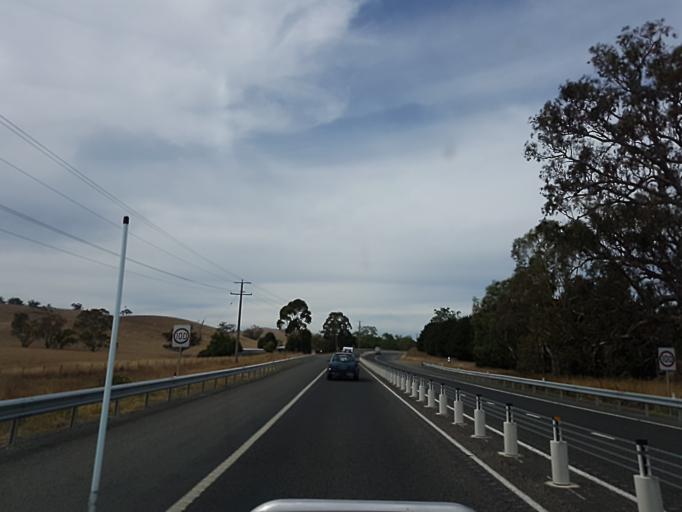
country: AU
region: Victoria
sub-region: Murrindindi
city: Alexandra
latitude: -37.2024
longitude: 145.4649
